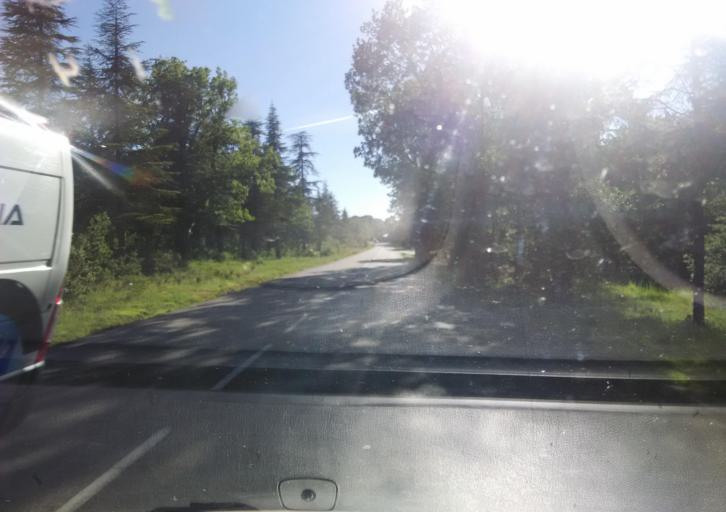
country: FR
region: Provence-Alpes-Cote d'Azur
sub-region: Departement du Var
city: Vinon-sur-Verdon
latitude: 43.7158
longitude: 5.7844
